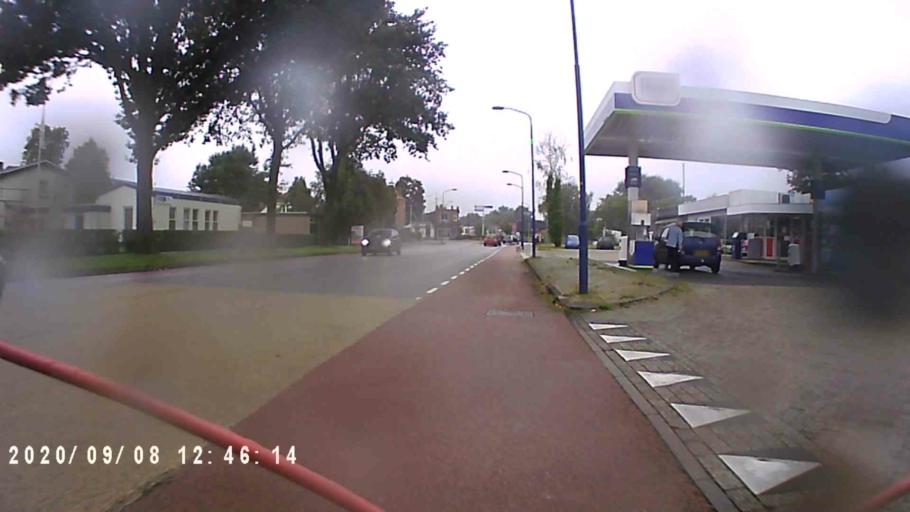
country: NL
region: Groningen
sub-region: Gemeente Veendam
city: Veendam
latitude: 53.1100
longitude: 6.8874
